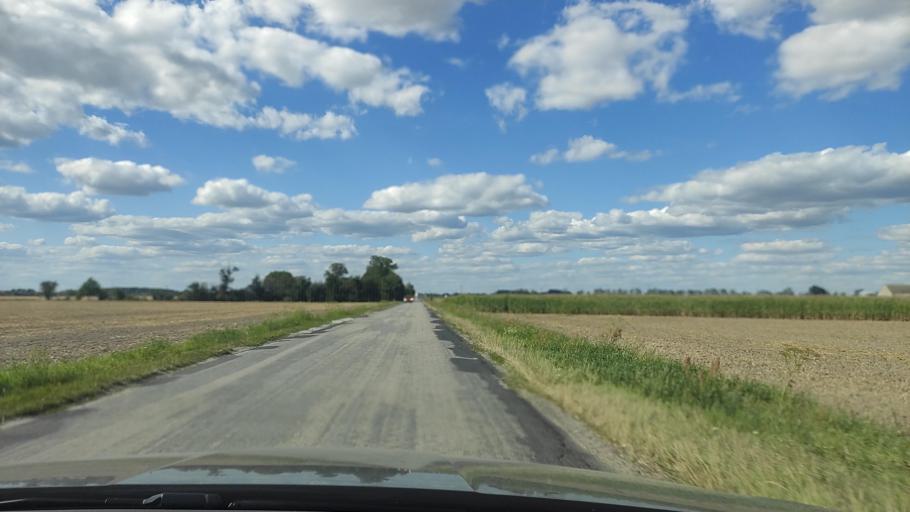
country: PL
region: Greater Poland Voivodeship
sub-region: Powiat poznanski
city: Kleszczewo
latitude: 52.3596
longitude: 17.1705
